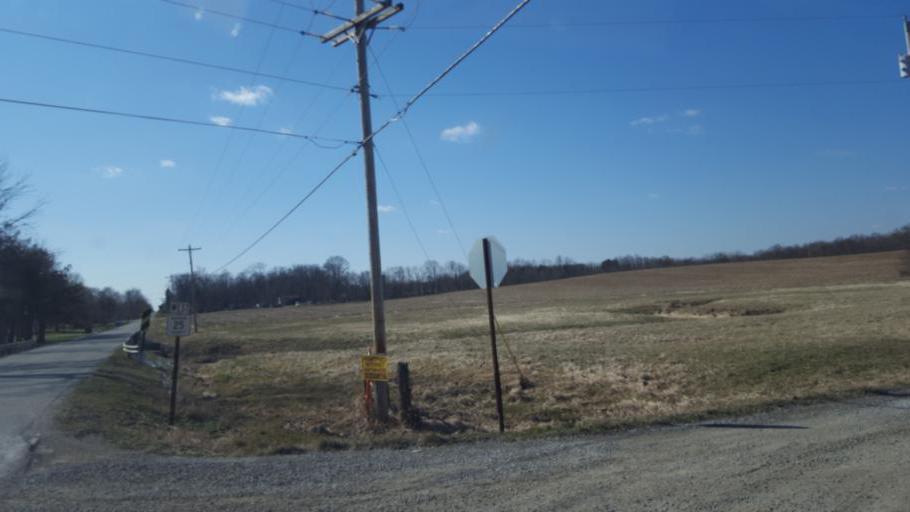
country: US
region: Ohio
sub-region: Morrow County
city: Mount Gilead
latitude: 40.4595
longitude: -82.7453
